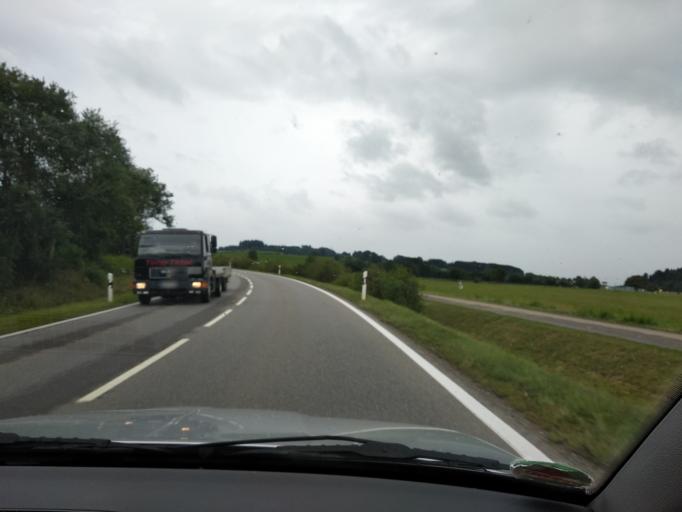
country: DE
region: Baden-Wuerttemberg
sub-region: Tuebingen Region
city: Leutkirch im Allgau
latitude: 47.8170
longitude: 9.9896
